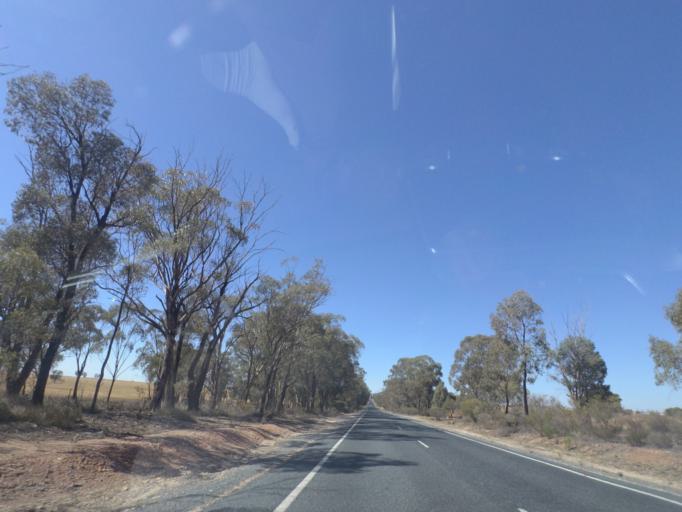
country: AU
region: New South Wales
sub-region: Bland
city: West Wyalong
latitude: -34.1467
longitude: 147.1192
